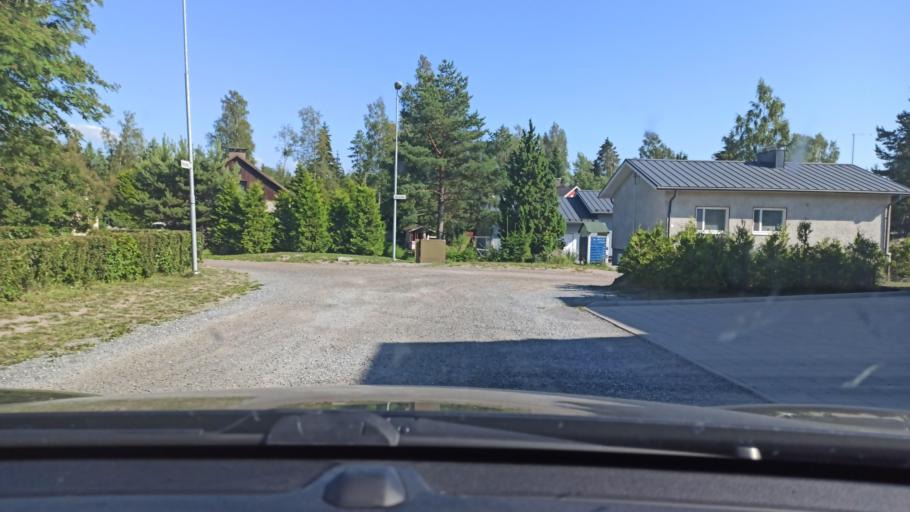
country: FI
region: Satakunta
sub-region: Pori
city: Noormarkku
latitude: 61.5116
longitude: 21.8692
